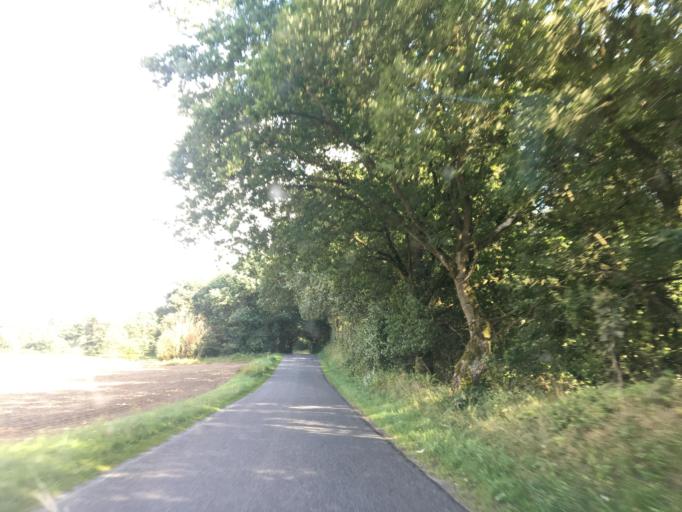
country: DK
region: South Denmark
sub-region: Middelfart Kommune
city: Ejby
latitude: 55.3922
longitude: 9.9290
